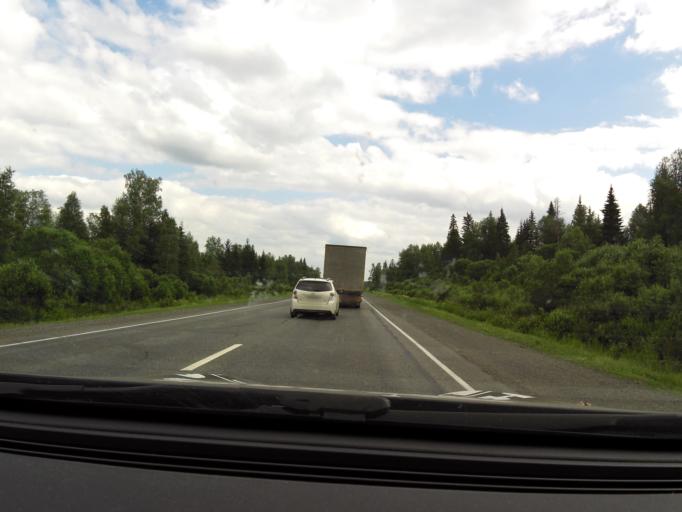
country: RU
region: Sverdlovsk
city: Atig
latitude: 56.8112
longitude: 59.3627
